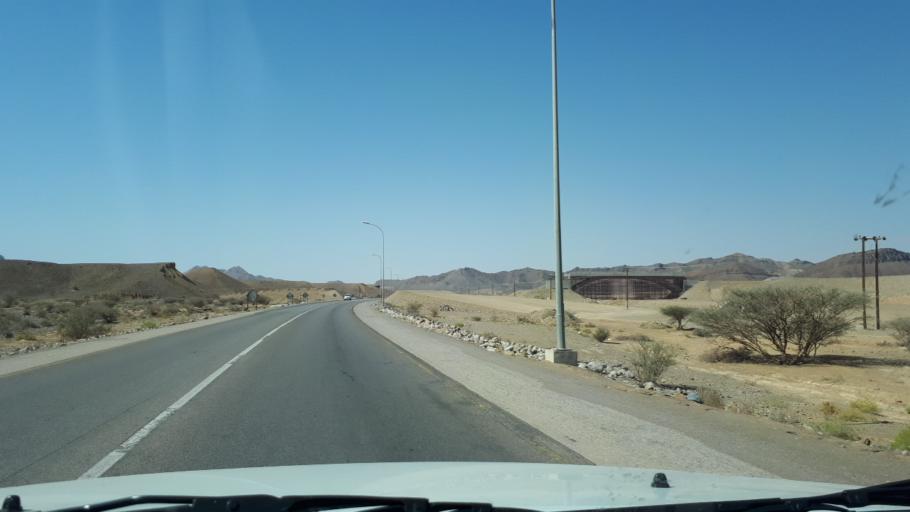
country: OM
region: Ash Sharqiyah
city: Sur
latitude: 22.3780
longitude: 59.3204
